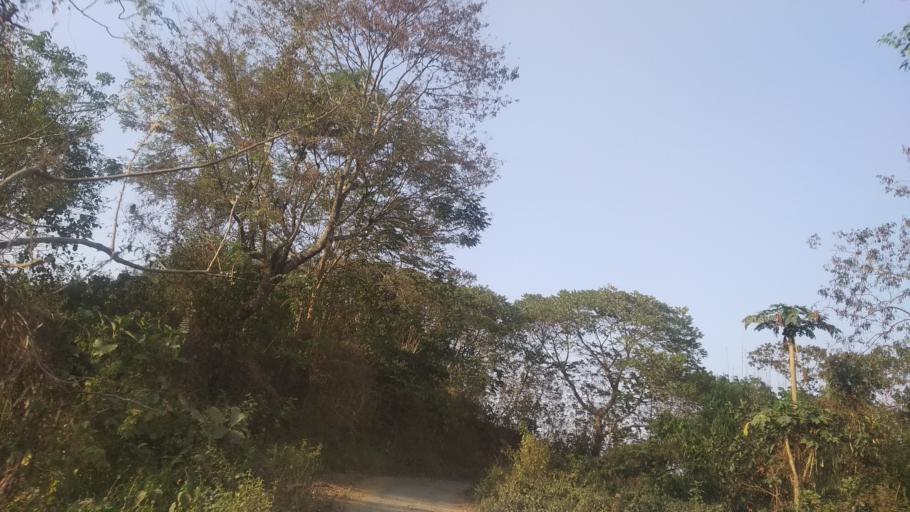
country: IN
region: Tripura
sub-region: West Tripura
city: Sonamura
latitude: 23.4369
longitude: 91.3593
